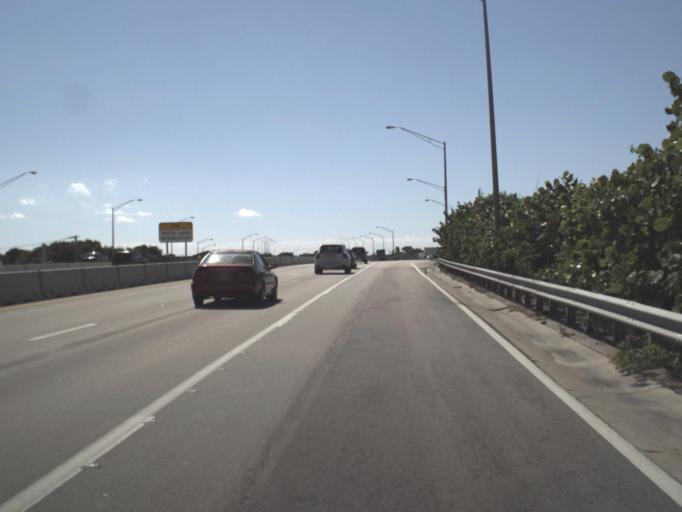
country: US
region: Florida
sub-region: Miami-Dade County
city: Cutler Ridge
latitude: 25.5781
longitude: -80.3651
